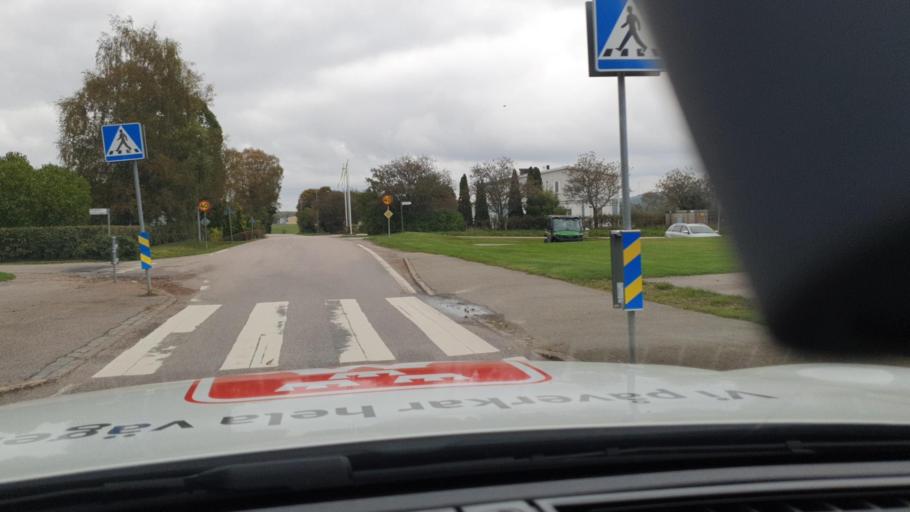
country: SE
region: Halland
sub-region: Halmstads Kommun
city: Getinge
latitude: 56.9752
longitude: 12.6712
